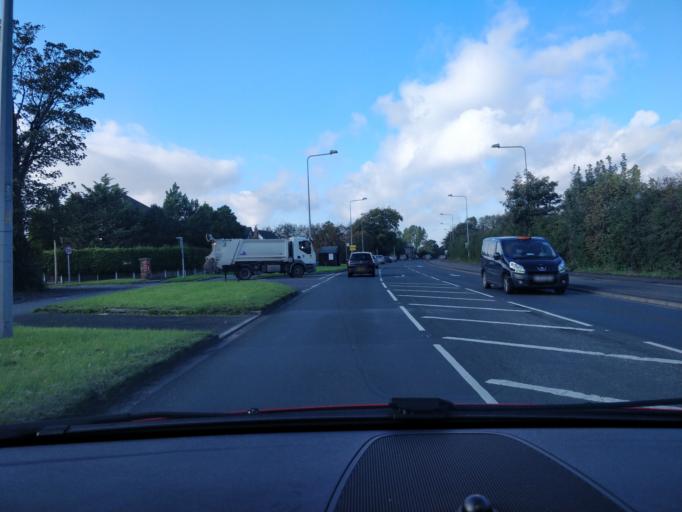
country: GB
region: England
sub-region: Sefton
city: Southport
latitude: 53.6236
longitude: -2.9606
